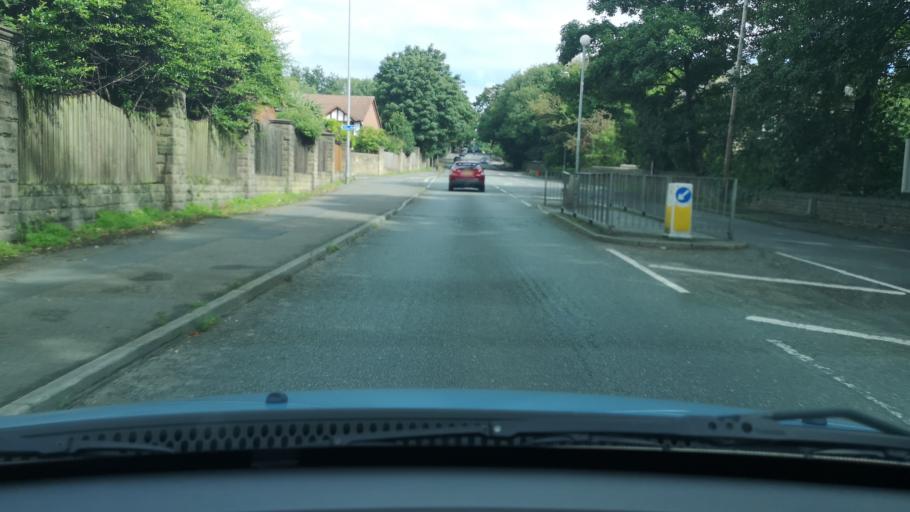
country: GB
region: England
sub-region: Kirklees
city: Heckmondwike
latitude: 53.7121
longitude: -1.6836
